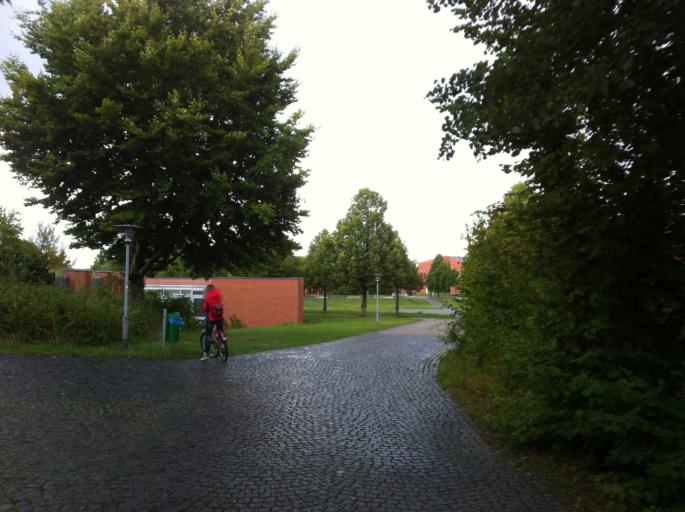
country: DE
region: Bavaria
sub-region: Upper Franconia
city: Bayreuth
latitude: 49.9279
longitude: 11.5855
